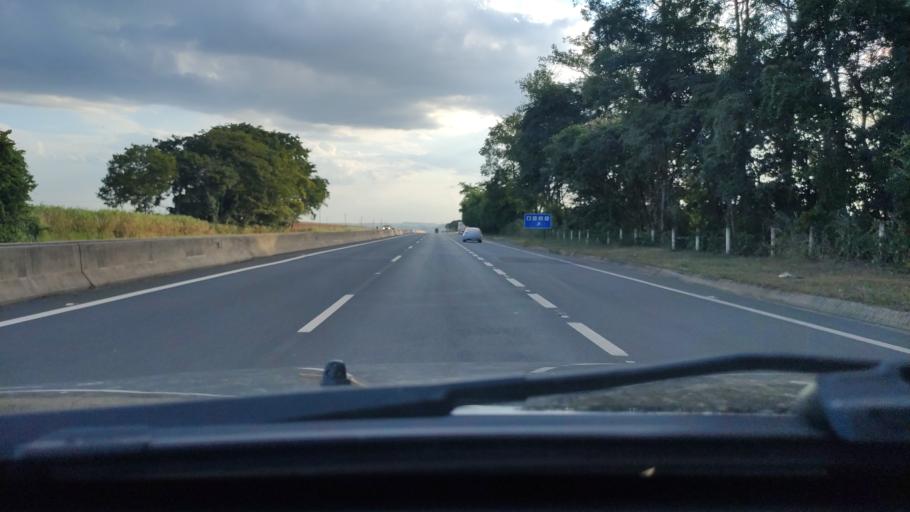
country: BR
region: Sao Paulo
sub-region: Artur Nogueira
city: Artur Nogueira
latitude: -22.4689
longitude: -47.1140
